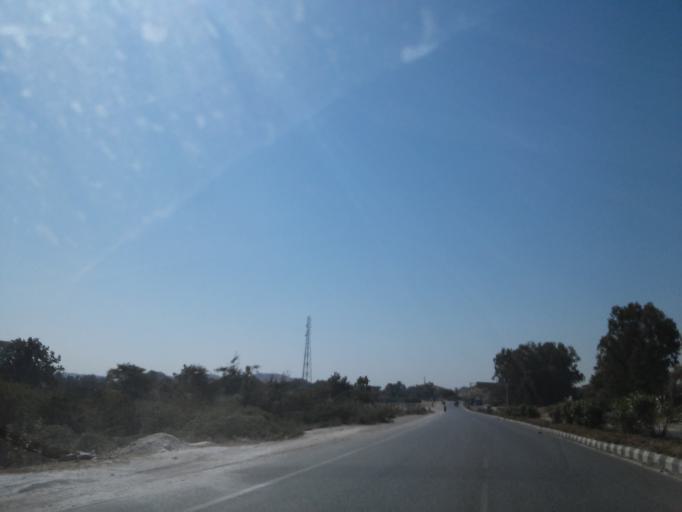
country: IN
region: Rajasthan
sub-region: Dungarpur
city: Dungarpur
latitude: 23.9215
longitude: 73.5649
